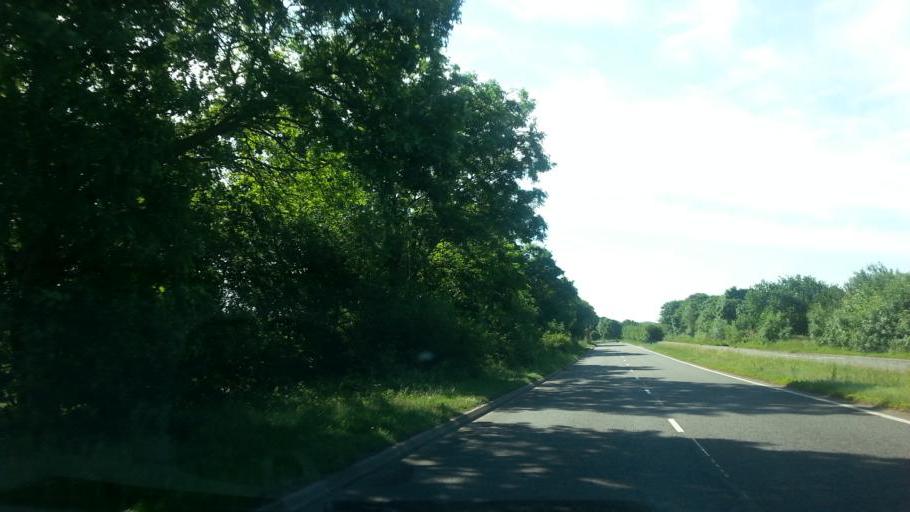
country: GB
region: England
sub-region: Hertfordshire
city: Shenley AV
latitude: 51.7227
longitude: -0.2862
